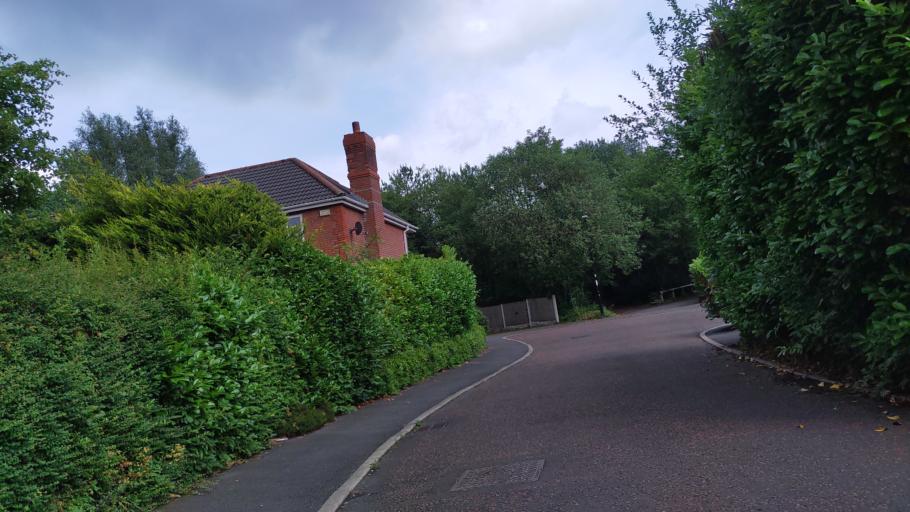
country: GB
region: England
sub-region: Lancashire
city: Chorley
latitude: 53.6784
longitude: -2.6306
